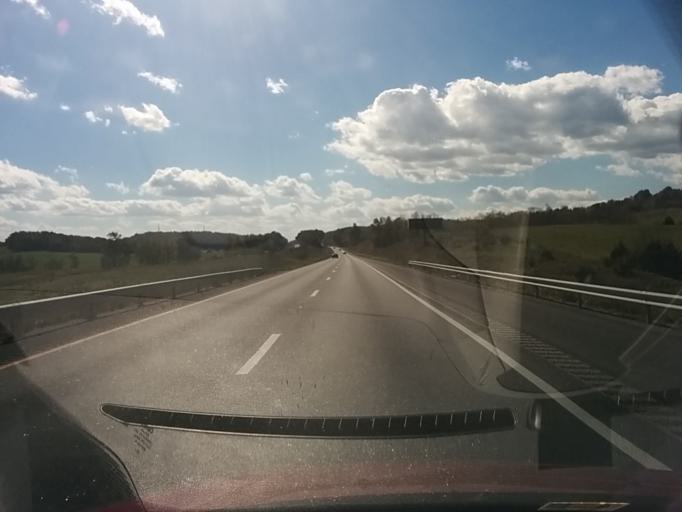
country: US
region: Virginia
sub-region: City of Buena Vista
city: Buena Vista
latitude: 37.9188
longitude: -79.2486
